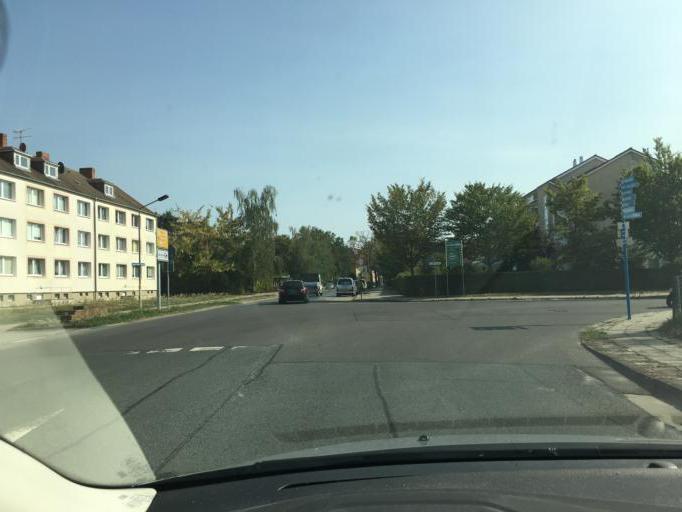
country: DE
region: Saxony-Anhalt
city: Barby
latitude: 51.9730
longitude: 11.8832
